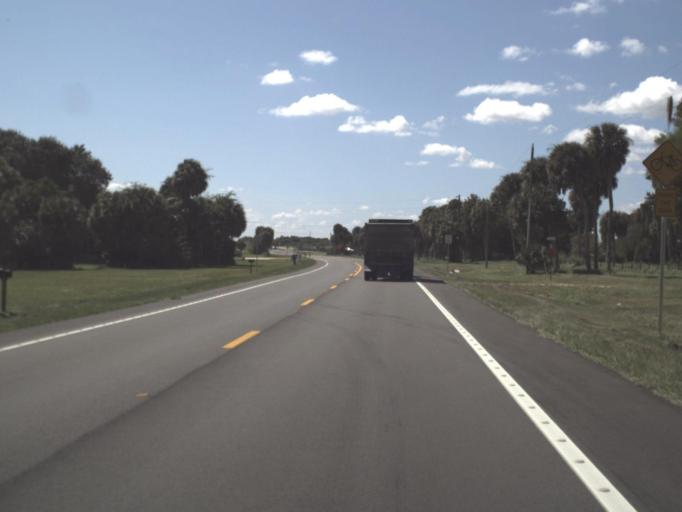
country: US
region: Florida
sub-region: Glades County
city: Moore Haven
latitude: 27.0027
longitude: -81.0624
